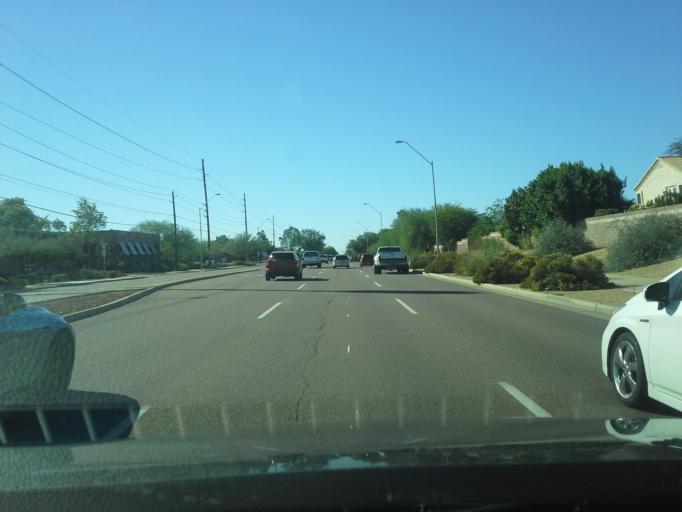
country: US
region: Arizona
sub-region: Maricopa County
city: Paradise Valley
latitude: 33.6406
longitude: -111.9614
